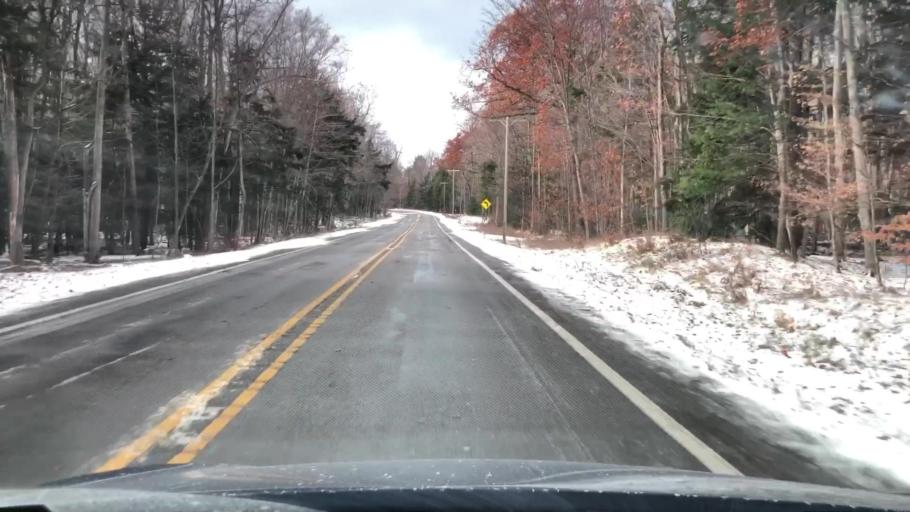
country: US
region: Michigan
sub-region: Antrim County
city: Elk Rapids
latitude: 44.9899
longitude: -85.4867
